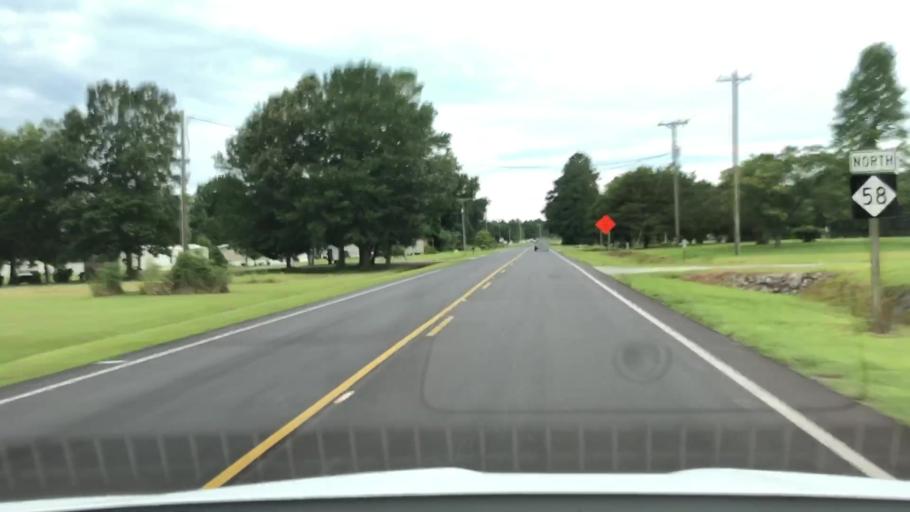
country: US
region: North Carolina
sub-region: Jones County
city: Maysville
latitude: 34.8802
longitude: -77.2061
